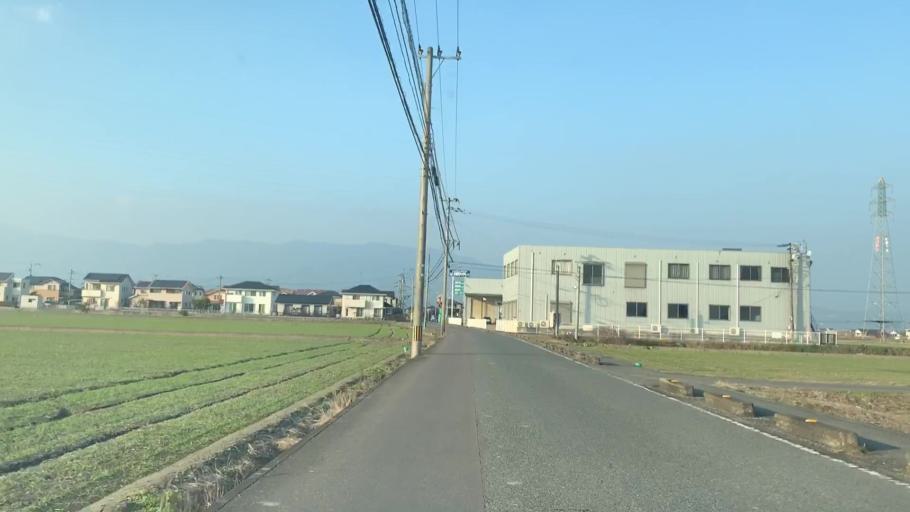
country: JP
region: Saga Prefecture
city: Saga-shi
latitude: 33.2670
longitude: 130.2304
